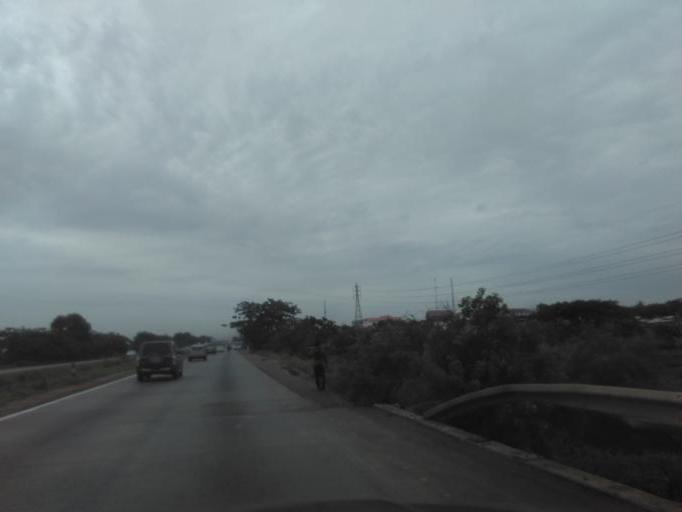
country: GH
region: Greater Accra
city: Tema
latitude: 5.6756
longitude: -0.0419
